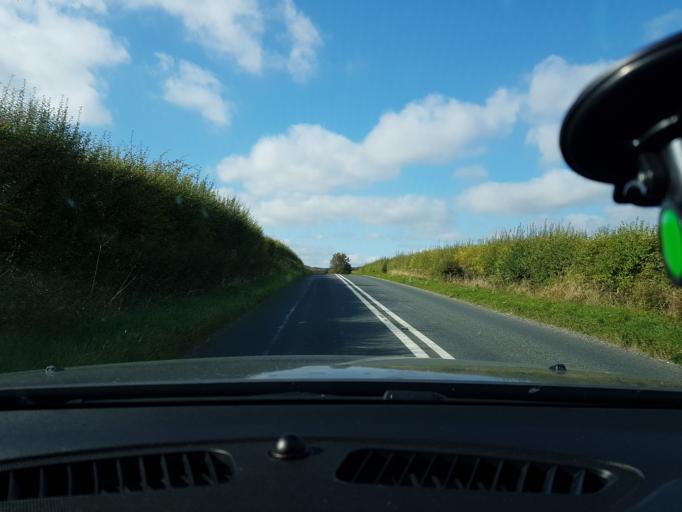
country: GB
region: England
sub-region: Wiltshire
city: Aldbourne
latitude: 51.5013
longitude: -1.6621
